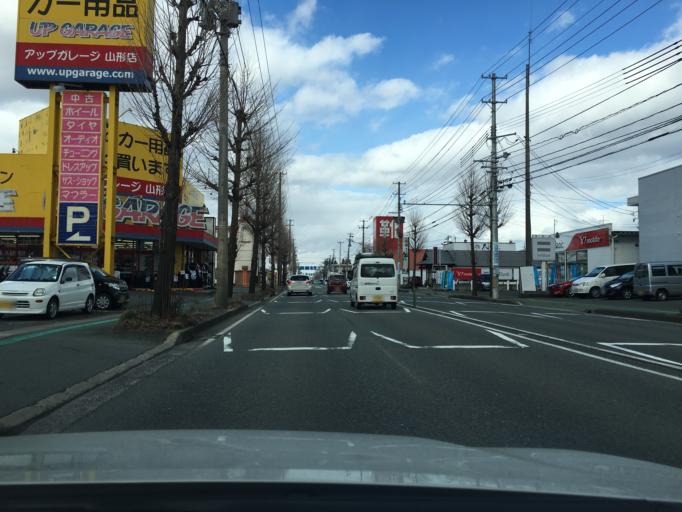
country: JP
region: Yamagata
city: Yamagata-shi
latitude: 38.2410
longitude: 140.3073
